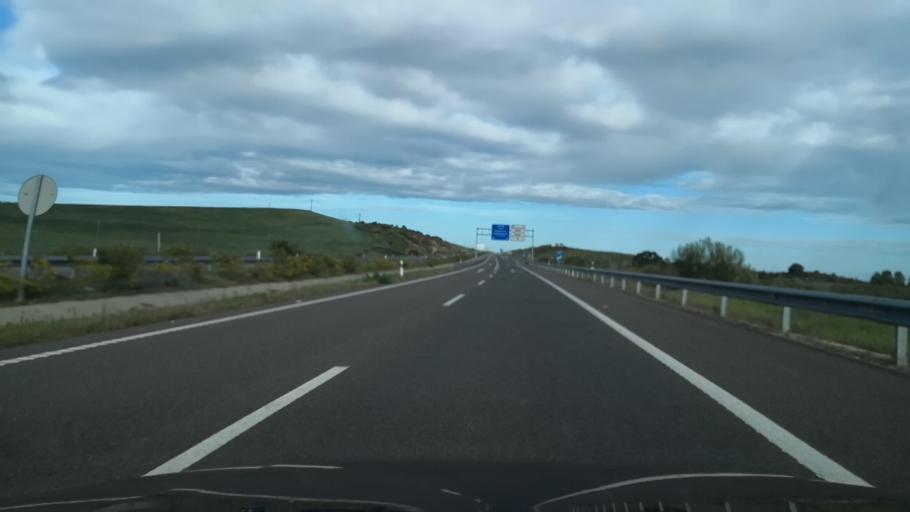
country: ES
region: Extremadura
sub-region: Provincia de Caceres
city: Casas de Don Gomez
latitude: 40.0112
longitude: -6.5699
